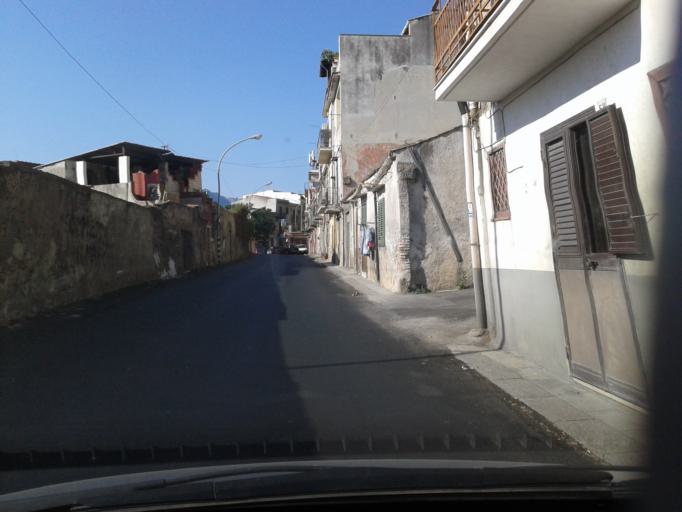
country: IT
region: Sicily
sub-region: Palermo
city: Monreale
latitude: 38.0954
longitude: 13.3094
